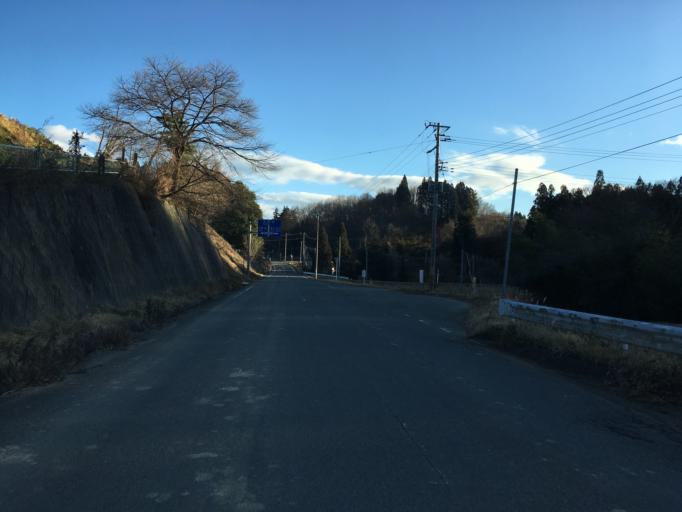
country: JP
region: Fukushima
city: Ishikawa
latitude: 37.1956
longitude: 140.5368
